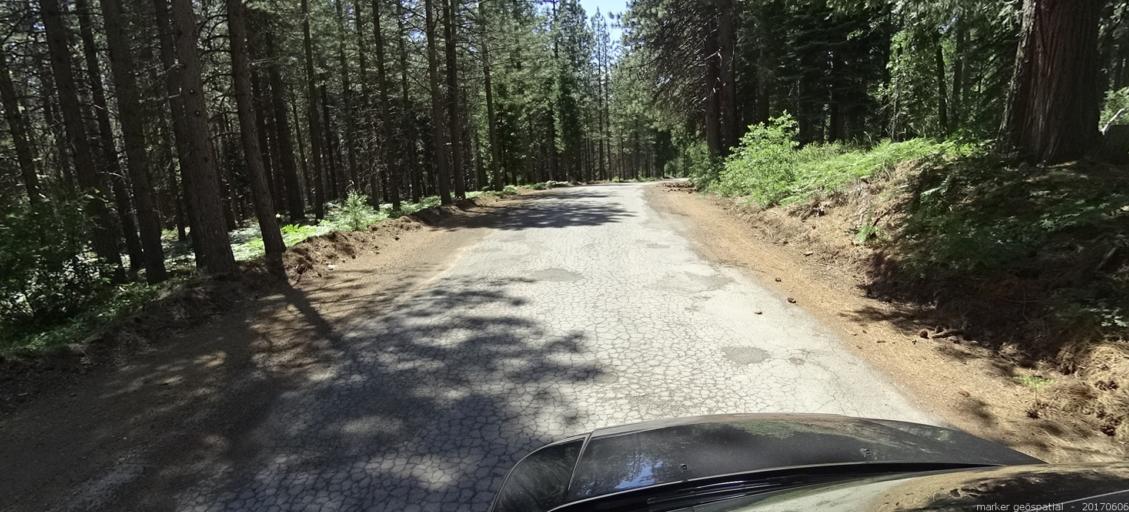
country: US
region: California
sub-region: Siskiyou County
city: Mount Shasta
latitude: 41.2741
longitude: -122.2948
